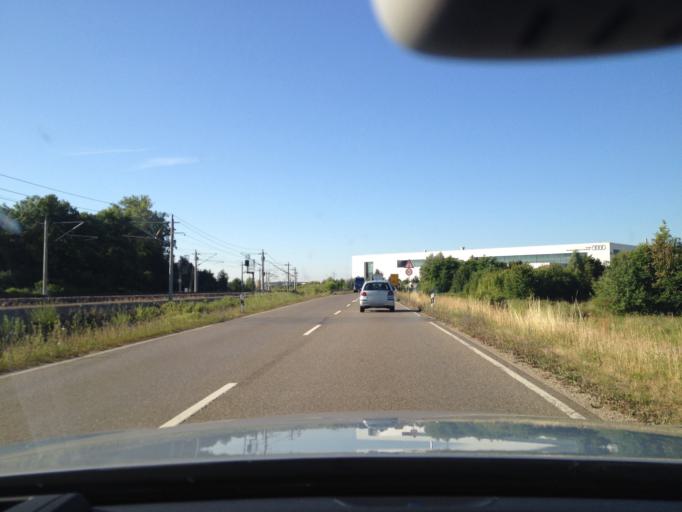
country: DE
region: Bavaria
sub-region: Upper Bavaria
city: Wettstetten
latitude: 48.7951
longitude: 11.4243
